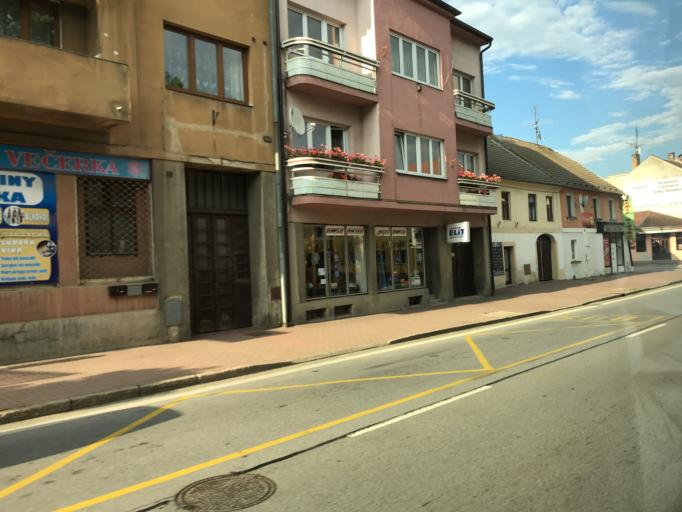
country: CZ
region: Jihocesky
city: Lisov
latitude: 49.0153
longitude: 14.6120
